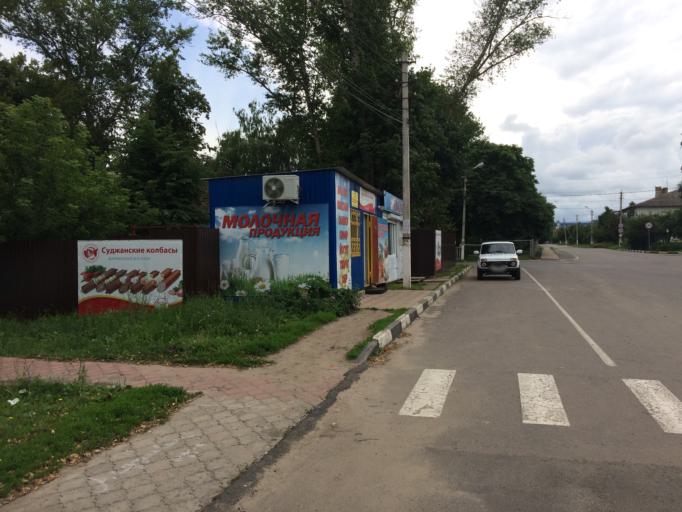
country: RU
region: Kursk
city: Zolotukhino
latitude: 51.9737
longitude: 36.3067
